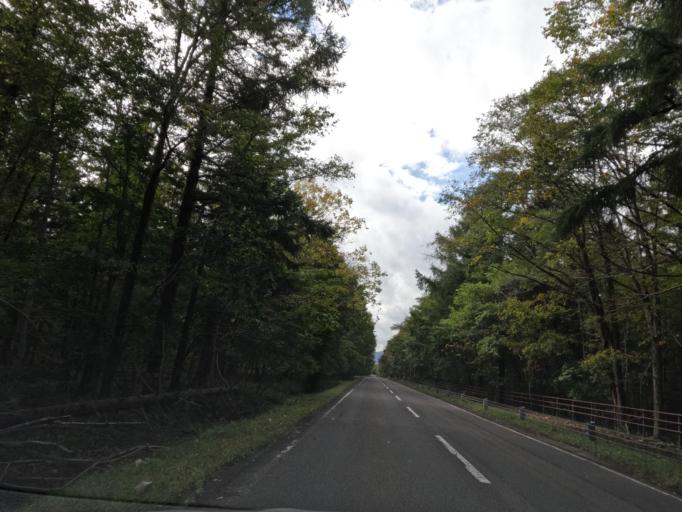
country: JP
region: Hokkaido
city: Chitose
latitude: 42.7916
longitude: 141.5350
